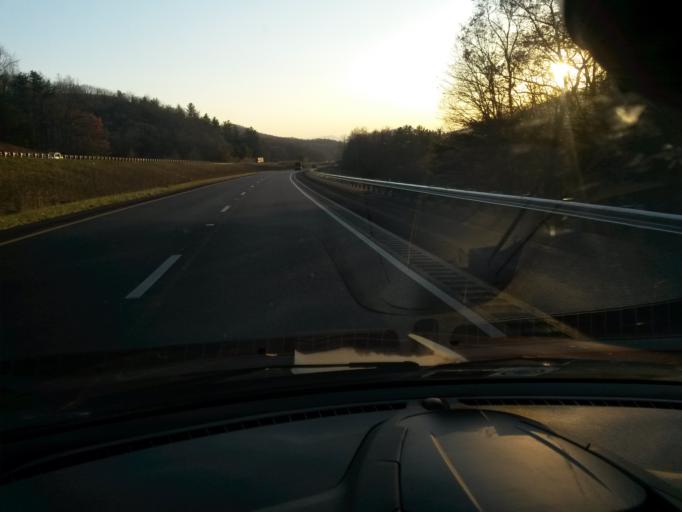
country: US
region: Virginia
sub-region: Alleghany County
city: Clifton Forge
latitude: 37.8507
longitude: -79.6316
